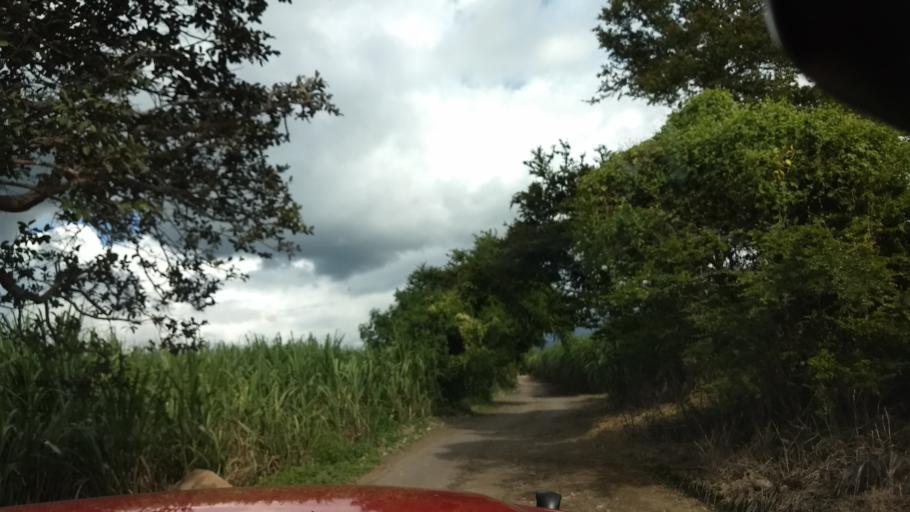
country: MX
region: Colima
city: Suchitlan
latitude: 19.4611
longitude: -103.7611
